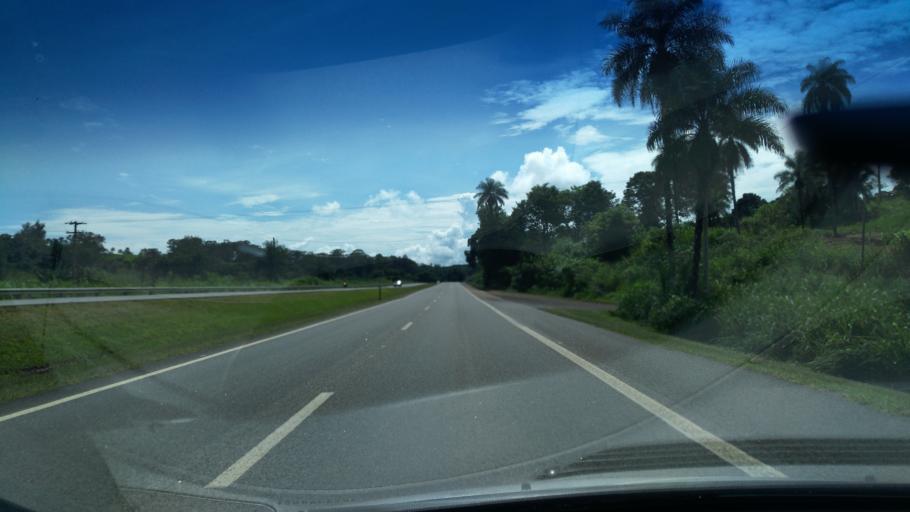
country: BR
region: Sao Paulo
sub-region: Santo Antonio Do Jardim
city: Espirito Santo do Pinhal
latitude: -22.2296
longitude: -46.7952
